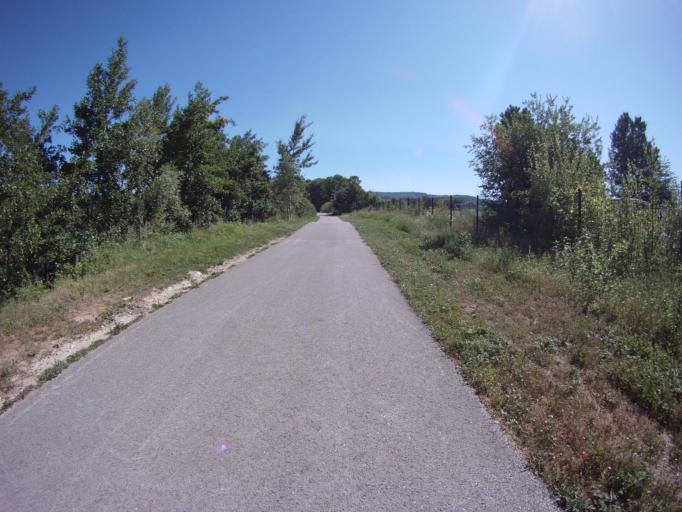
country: FR
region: Champagne-Ardenne
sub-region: Departement de la Marne
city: Dormans
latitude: 49.0816
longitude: 3.6388
